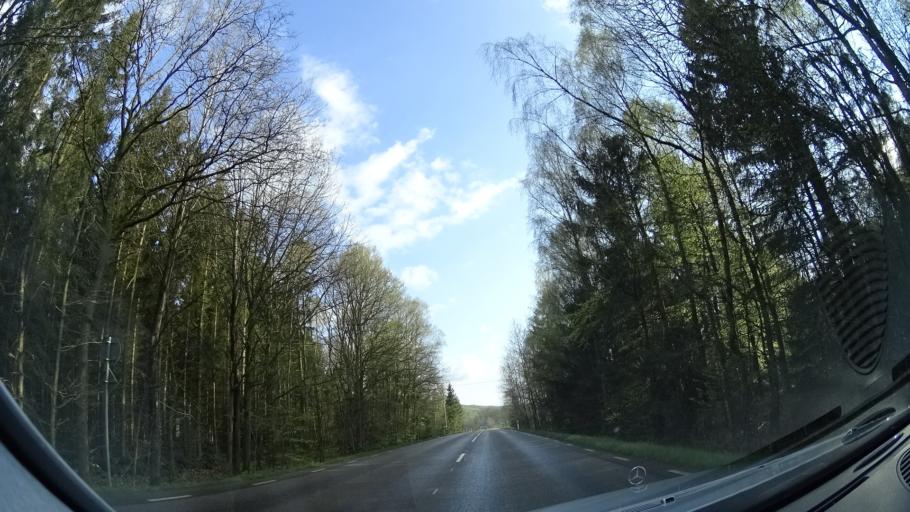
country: SE
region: Skane
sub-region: Klippans Kommun
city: Ljungbyhed
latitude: 56.0549
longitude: 13.2413
